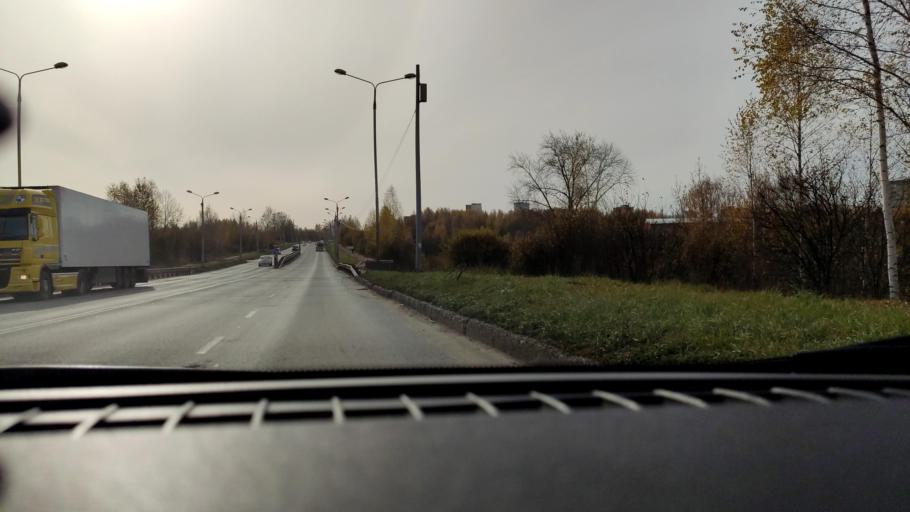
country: RU
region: Perm
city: Perm
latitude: 58.0713
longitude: 56.3672
